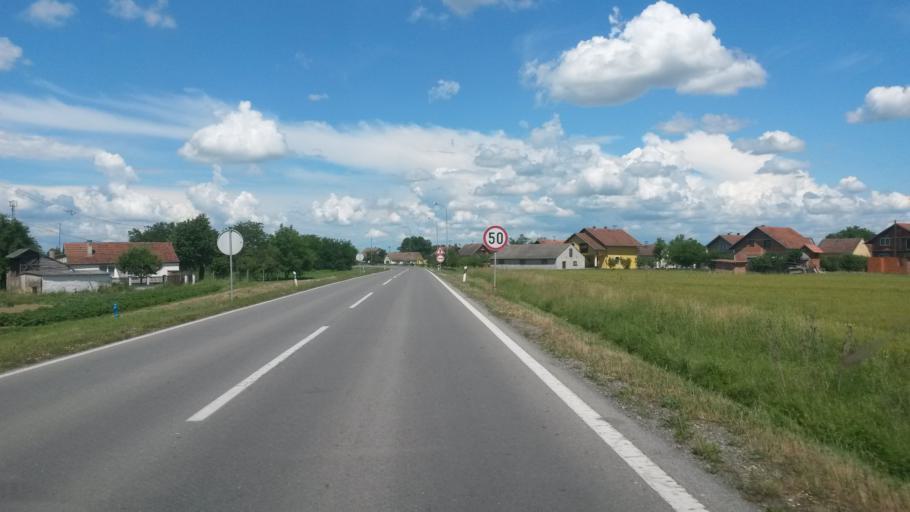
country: HR
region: Osjecko-Baranjska
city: Vuka
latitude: 45.4258
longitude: 18.4987
